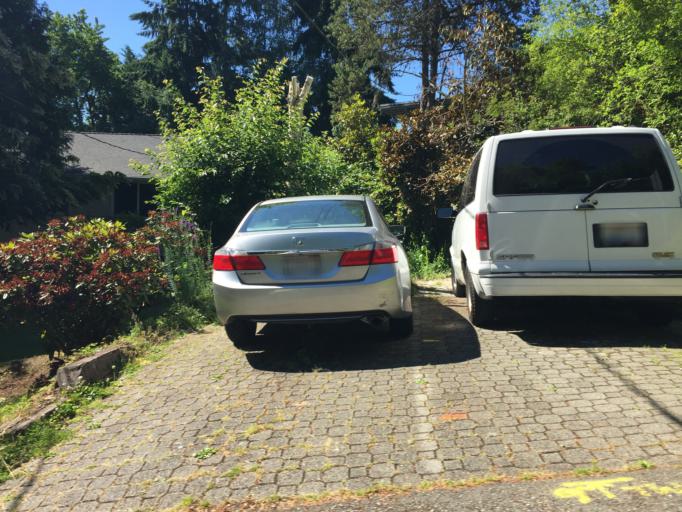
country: US
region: Washington
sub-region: King County
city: Clyde Hill
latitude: 47.6258
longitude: -122.2065
